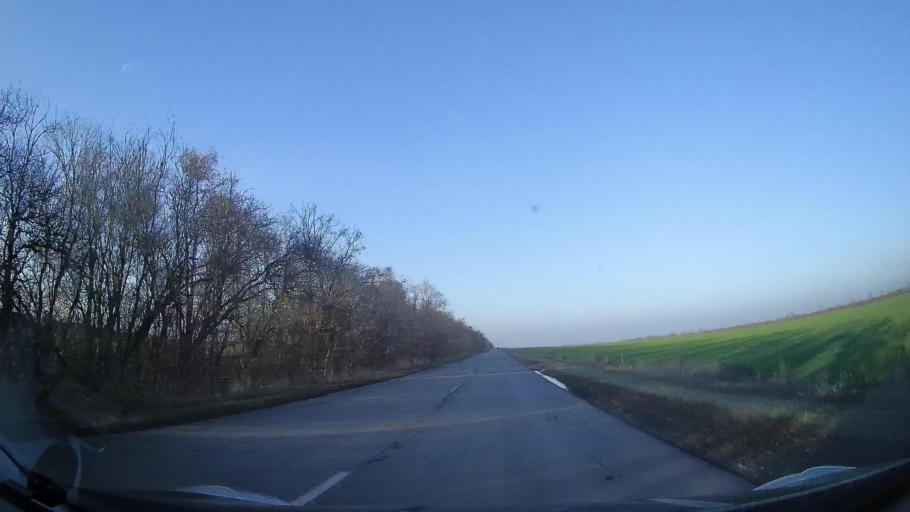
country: RU
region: Rostov
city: Kirovskaya
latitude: 47.0051
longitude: 39.9790
